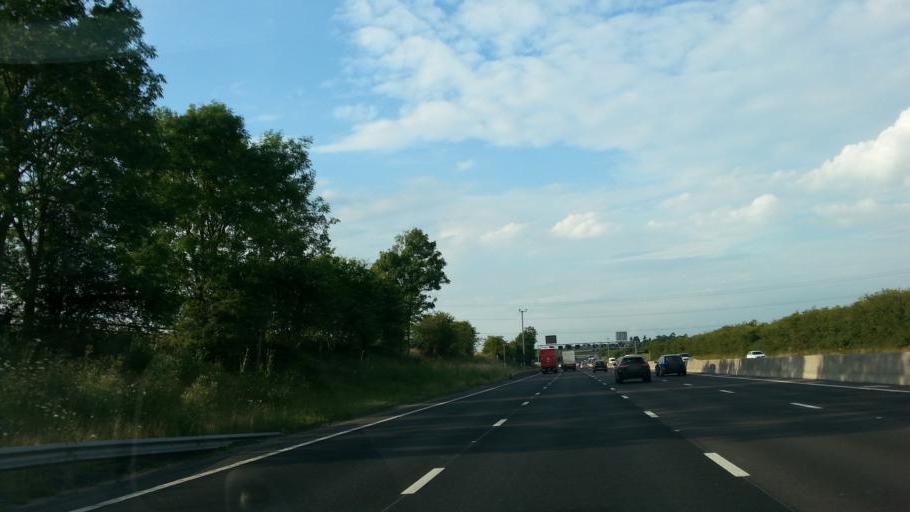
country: GB
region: England
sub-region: Worcestershire
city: Bromsgrove
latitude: 52.3137
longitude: -2.1004
